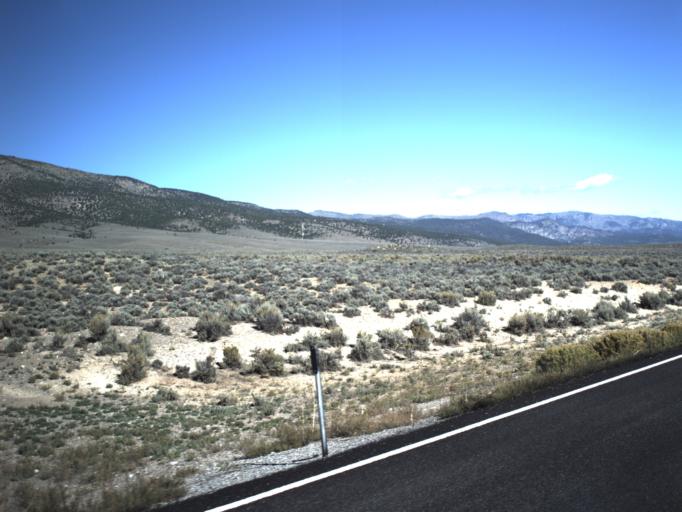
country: US
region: Utah
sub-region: Piute County
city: Junction
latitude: 38.2162
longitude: -112.0015
